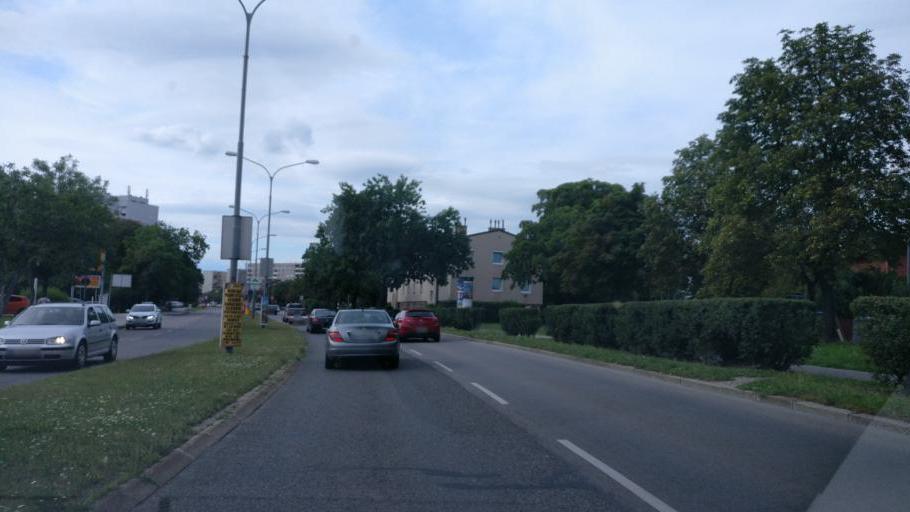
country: AT
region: Lower Austria
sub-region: Politischer Bezirk Wien-Umgebung
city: Gerasdorf bei Wien
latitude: 48.2346
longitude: 16.4435
